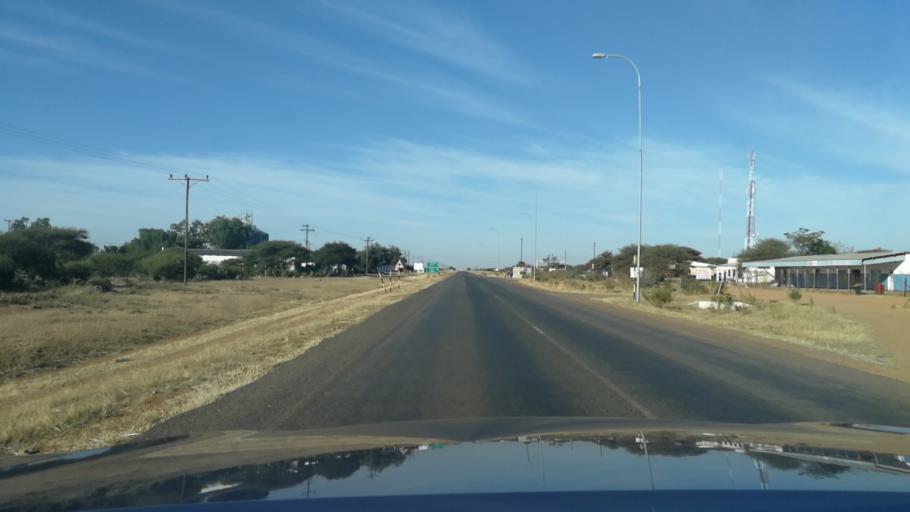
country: BW
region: South East
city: Janeng
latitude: -25.4695
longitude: 25.6002
